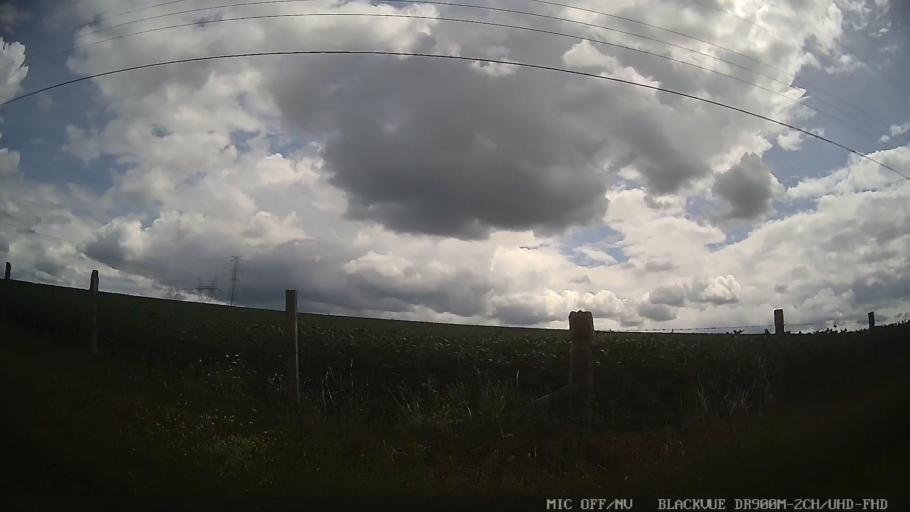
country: BR
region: Sao Paulo
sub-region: Suzano
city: Suzano
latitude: -23.6817
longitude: -46.2539
